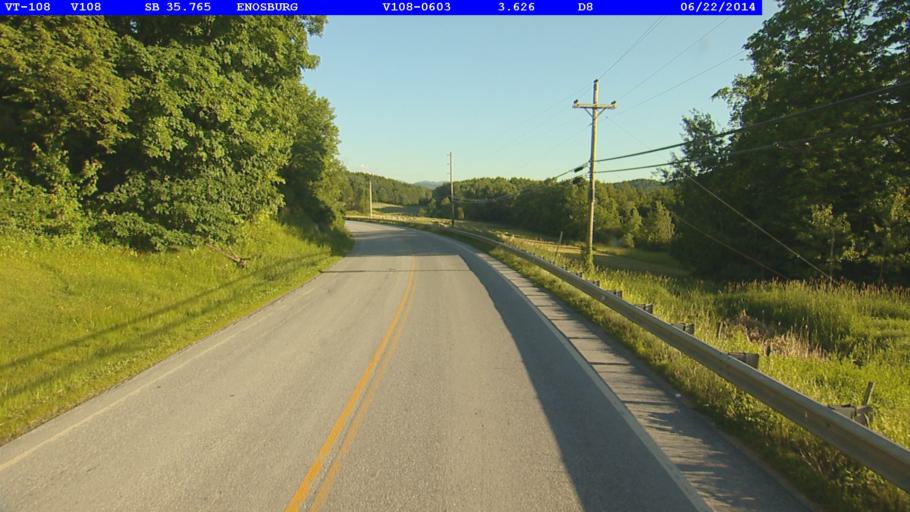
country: US
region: Vermont
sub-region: Franklin County
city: Enosburg Falls
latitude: 44.8878
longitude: -72.8028
